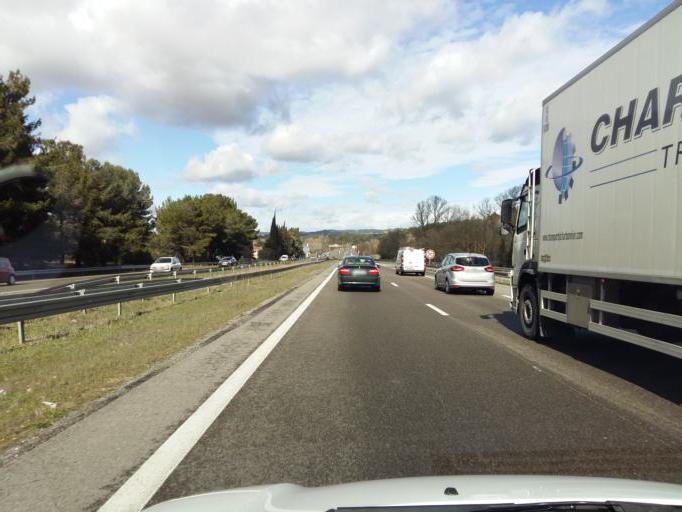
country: FR
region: Provence-Alpes-Cote d'Azur
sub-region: Departement des Bouches-du-Rhone
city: Bouc-Bel-Air
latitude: 43.4901
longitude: 5.4075
